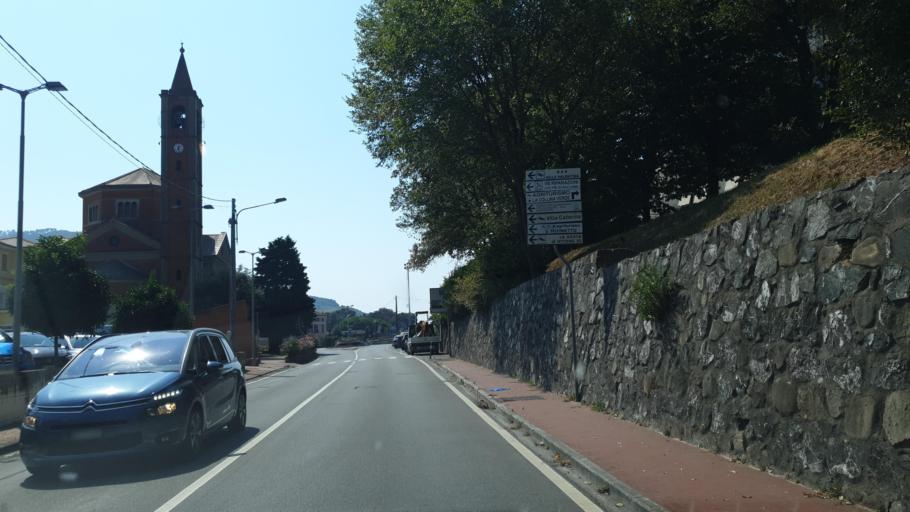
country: IT
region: Liguria
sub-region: Provincia di La Spezia
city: Levanto
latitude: 44.1765
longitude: 9.6201
